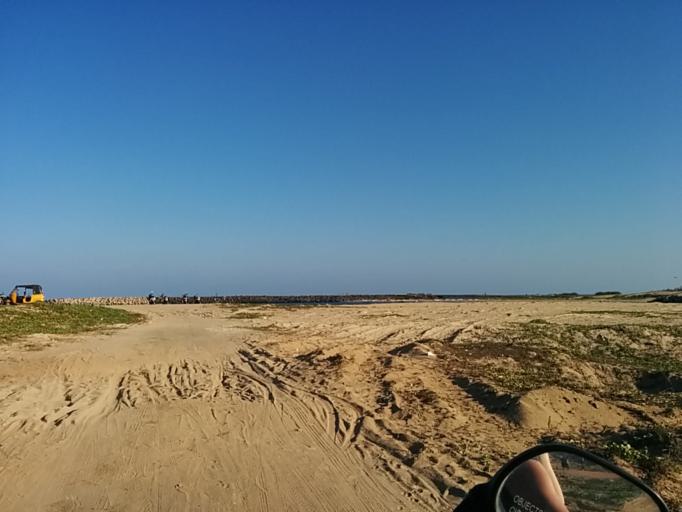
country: IN
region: Pondicherry
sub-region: Puducherry
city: Puducherry
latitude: 11.9076
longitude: 79.8291
